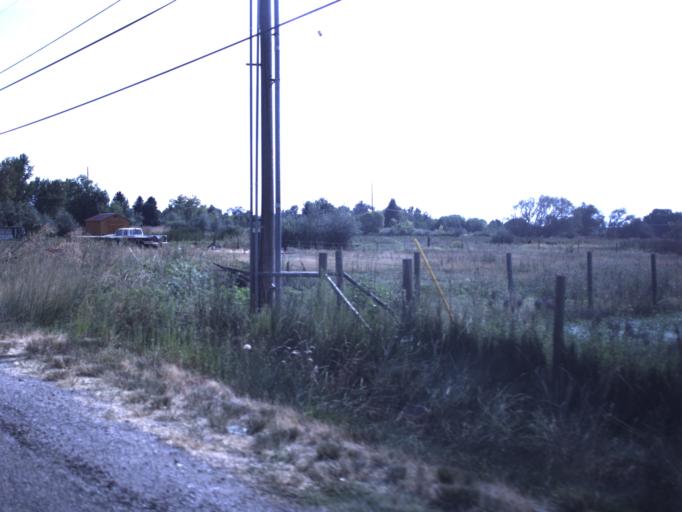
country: US
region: Utah
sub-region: Box Elder County
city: Brigham City
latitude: 41.5341
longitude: -112.0154
